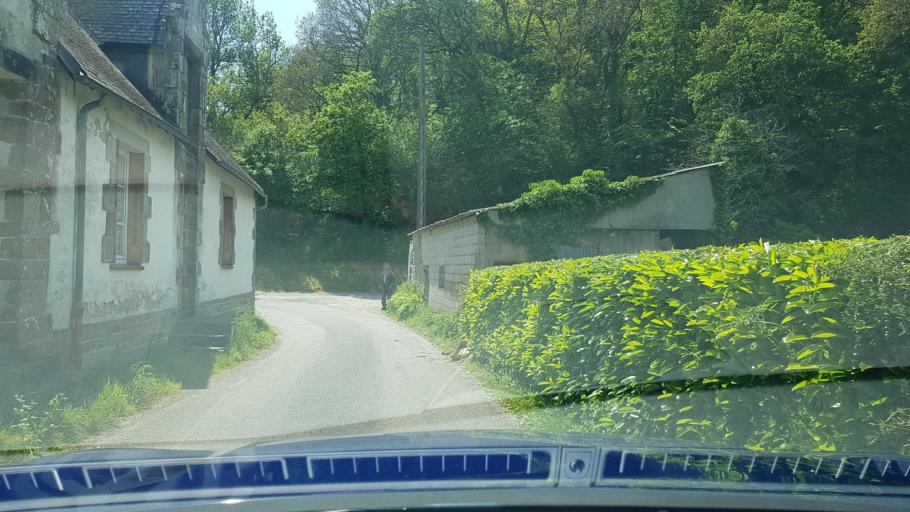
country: FR
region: Brittany
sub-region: Departement du Morbihan
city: Gestel
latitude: 47.8151
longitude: -3.4207
